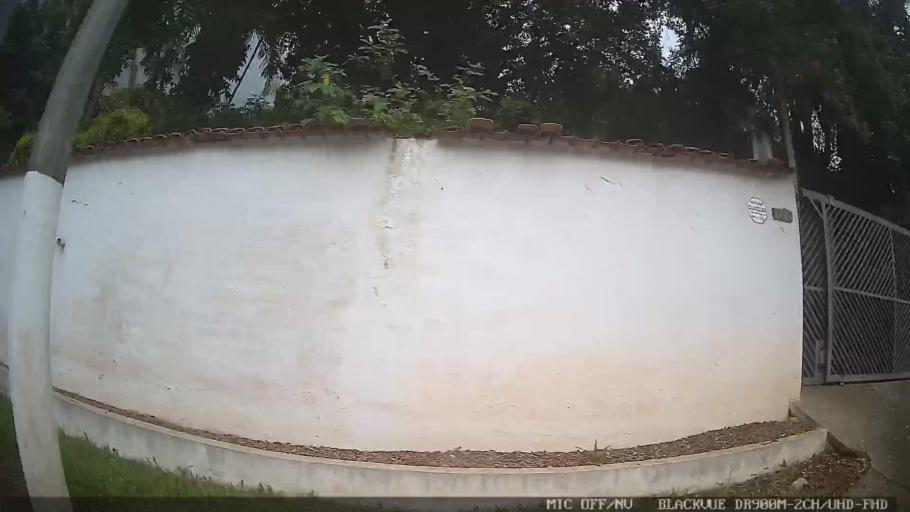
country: BR
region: Sao Paulo
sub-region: Atibaia
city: Atibaia
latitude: -23.1527
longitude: -46.5837
